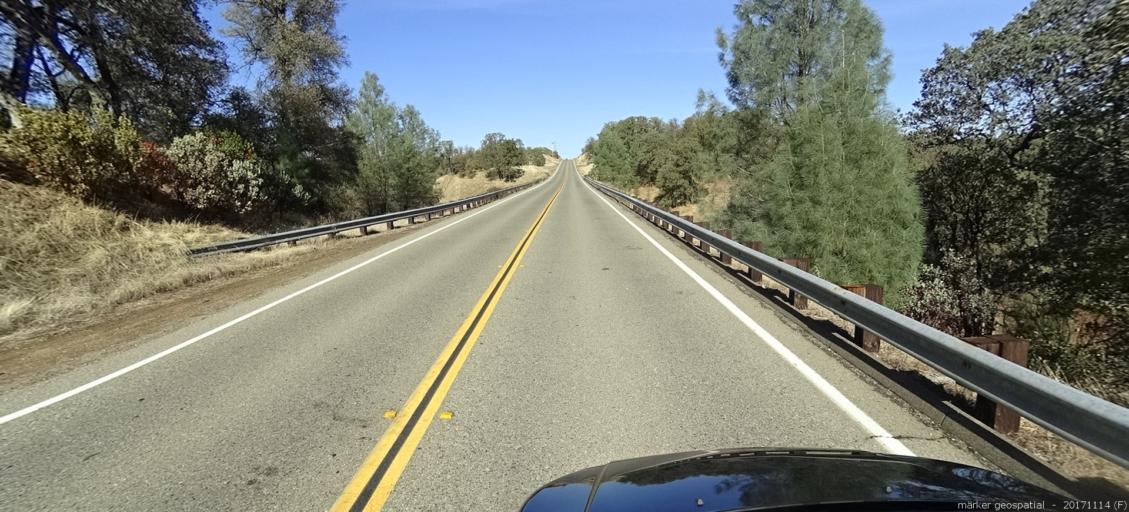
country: US
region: California
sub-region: Shasta County
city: Anderson
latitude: 40.4027
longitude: -122.4063
